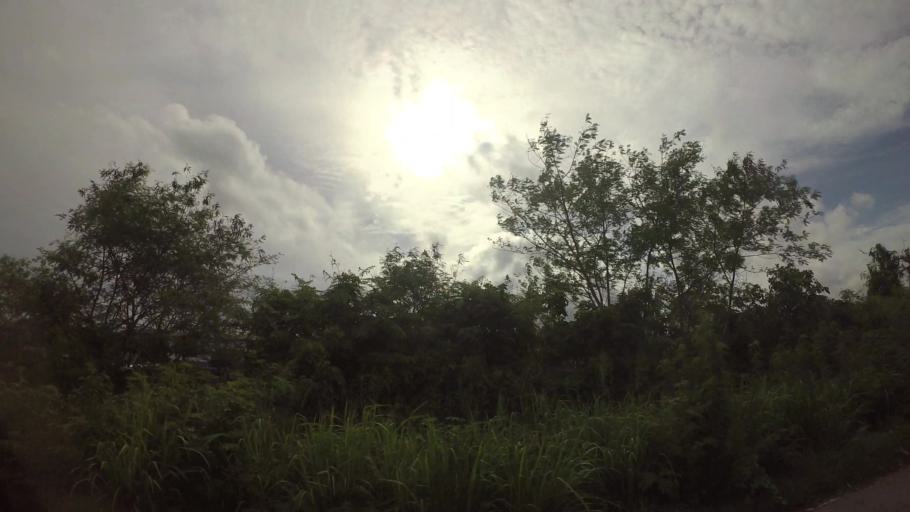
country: TH
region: Rayong
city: Rayong
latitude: 12.6625
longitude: 101.2794
